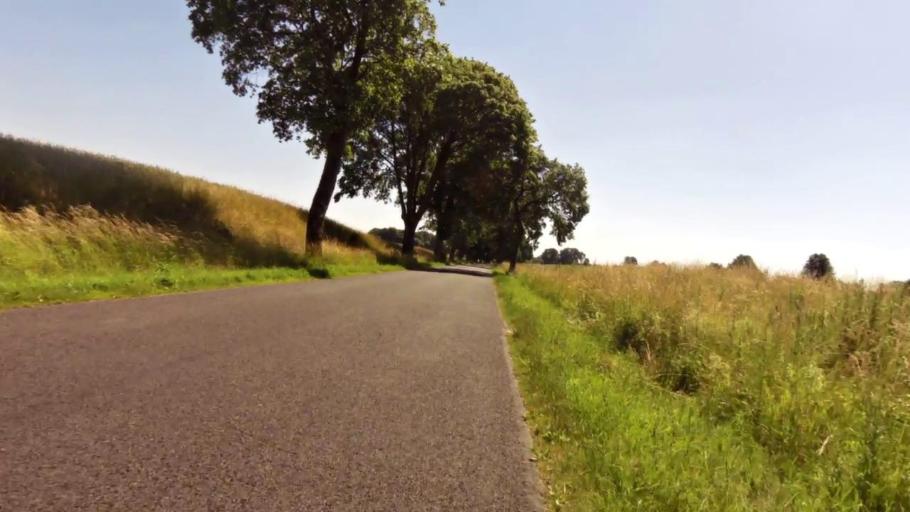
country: PL
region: West Pomeranian Voivodeship
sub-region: Powiat swidwinski
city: Rabino
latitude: 53.8498
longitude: 15.9846
